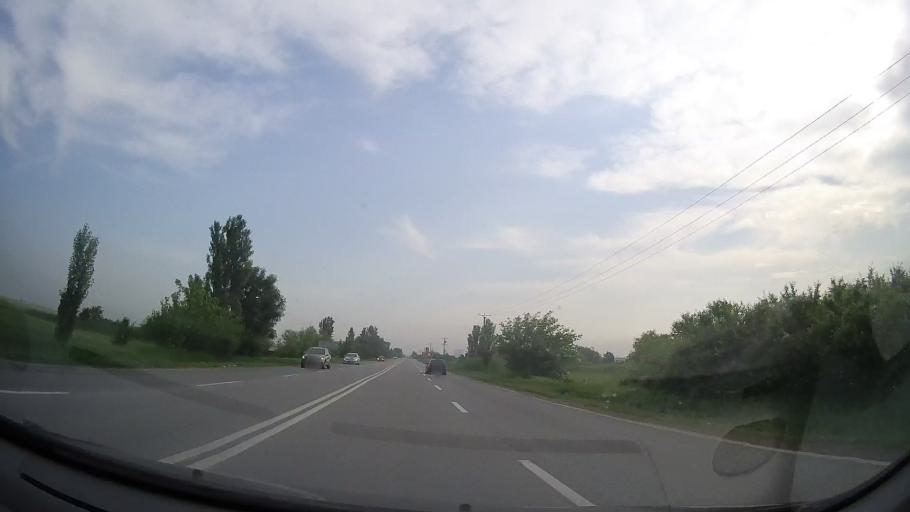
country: RO
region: Timis
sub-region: Comuna Sag
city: Sag
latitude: 45.6857
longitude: 21.1699
